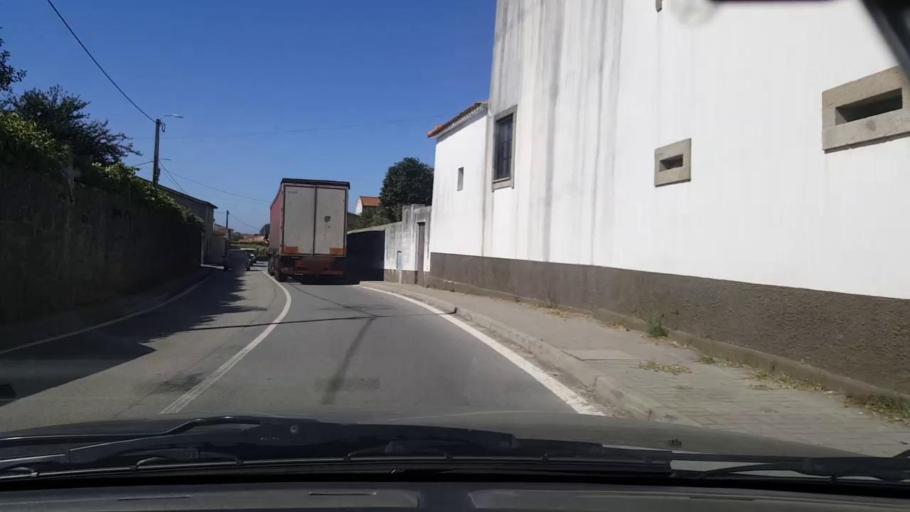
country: PT
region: Porto
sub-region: Vila do Conde
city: Arvore
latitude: 41.3406
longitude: -8.7003
